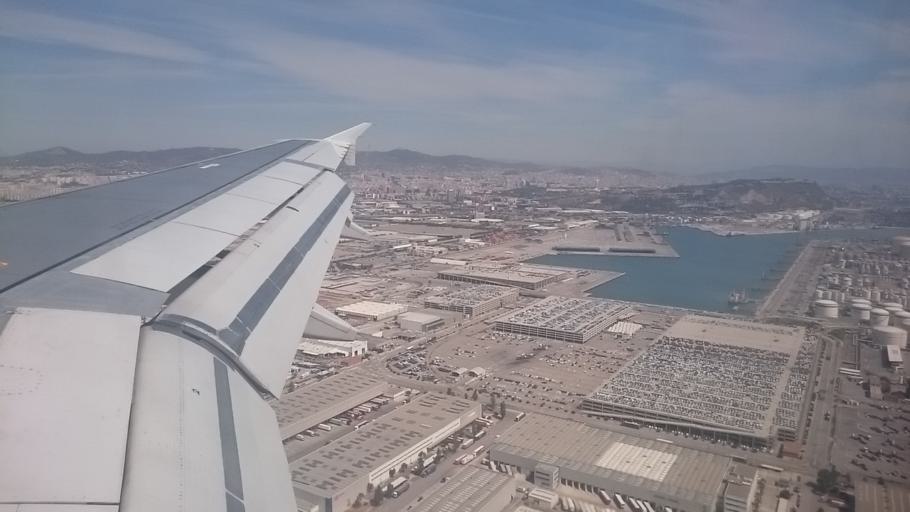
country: ES
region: Catalonia
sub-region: Provincia de Barcelona
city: El Prat de Llobregat
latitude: 41.3209
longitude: 2.1451
